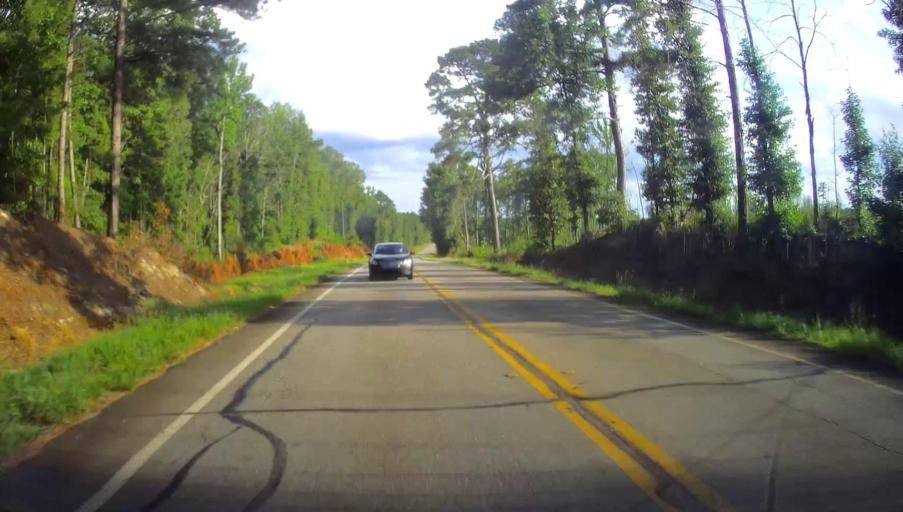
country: US
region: Georgia
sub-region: Crawford County
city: Knoxville
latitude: 32.8732
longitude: -83.9945
